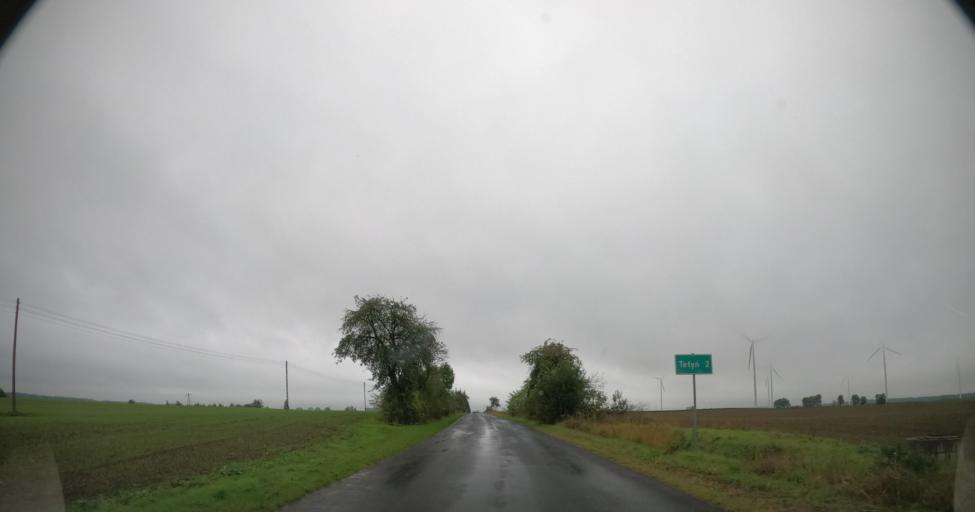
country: PL
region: West Pomeranian Voivodeship
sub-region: Powiat pyrzycki
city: Kozielice
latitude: 53.0664
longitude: 14.7847
